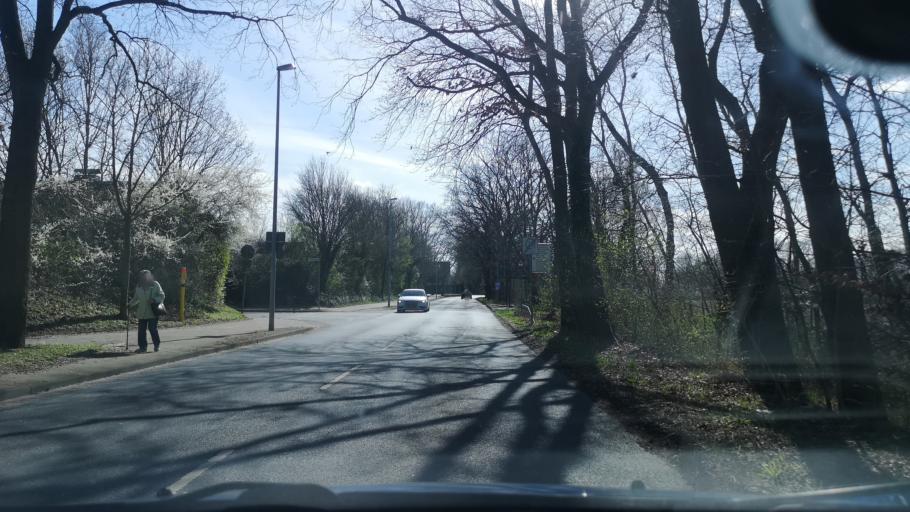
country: DE
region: Lower Saxony
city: Isernhagen Farster Bauerschaft
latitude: 52.4354
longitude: 9.8374
